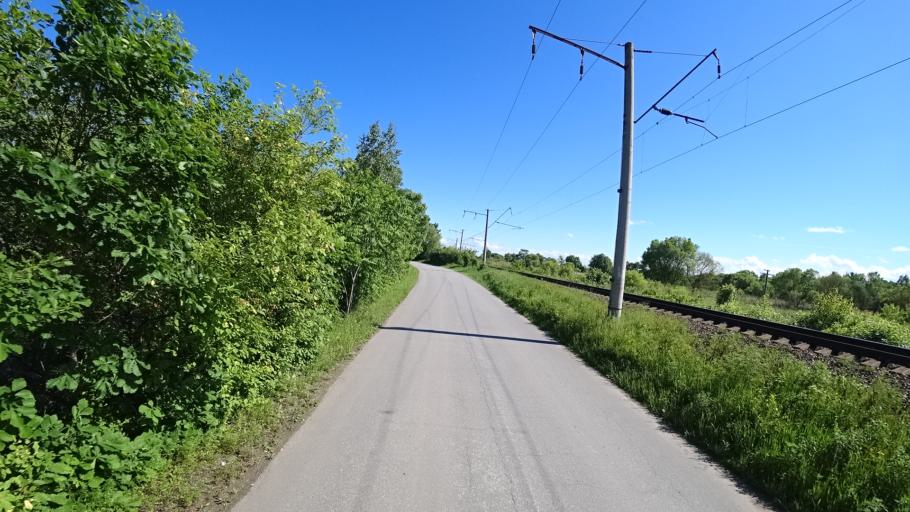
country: RU
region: Khabarovsk Krai
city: Khor
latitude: 47.8905
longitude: 135.0231
